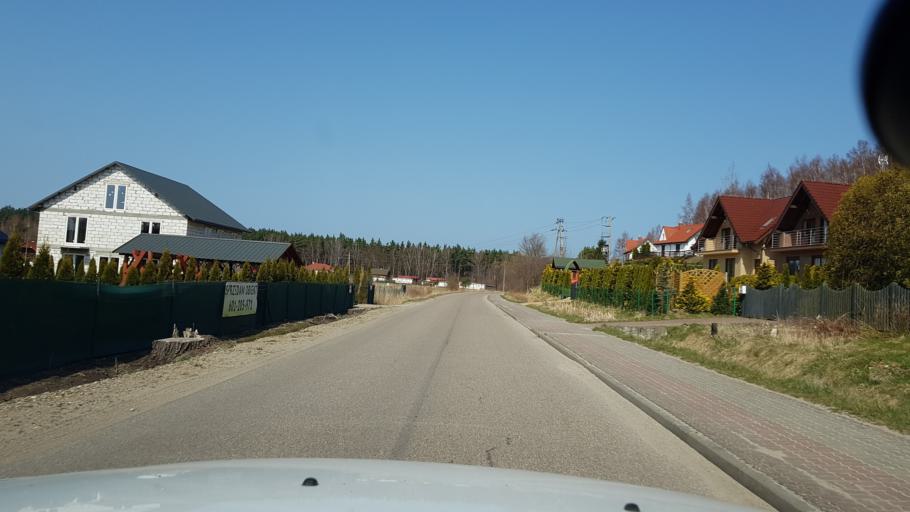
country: PL
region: West Pomeranian Voivodeship
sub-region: Powiat slawienski
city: Darlowo
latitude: 54.5165
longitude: 16.5149
